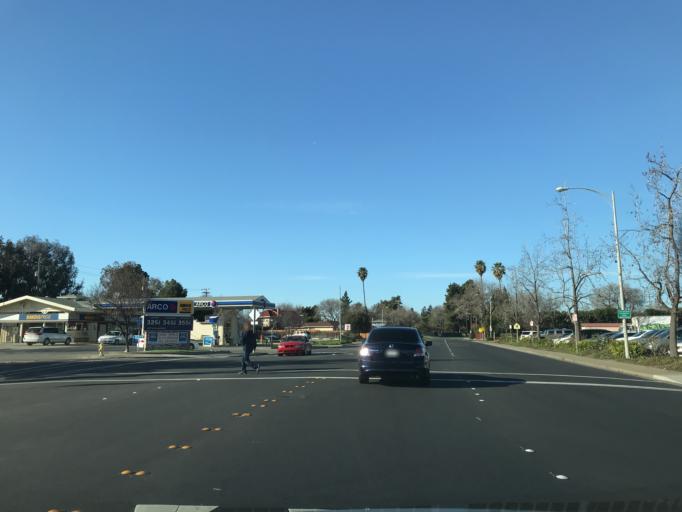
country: US
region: California
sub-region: Santa Clara County
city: Milpitas
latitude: 37.4275
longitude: -121.9136
